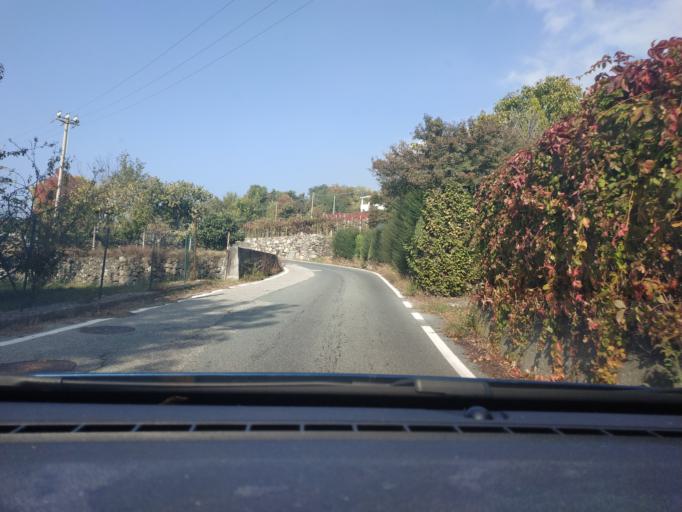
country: IT
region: Piedmont
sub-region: Provincia di Torino
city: Chiaverano
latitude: 45.5037
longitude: 7.9082
